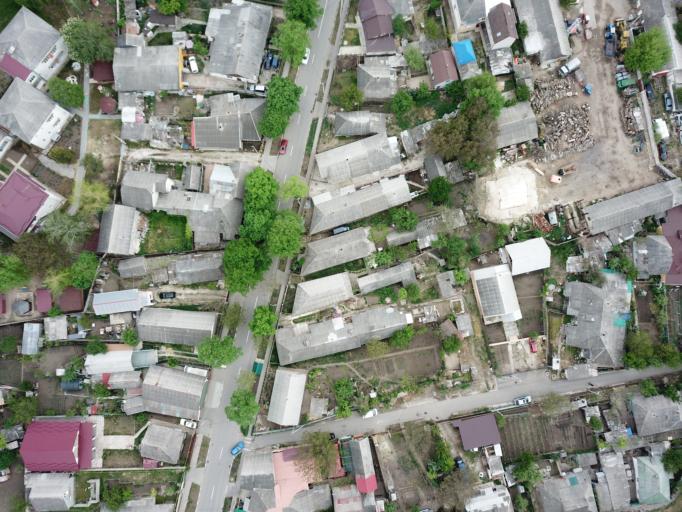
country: MD
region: Ungheni
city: Ungheni
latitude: 47.2064
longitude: 27.7946
